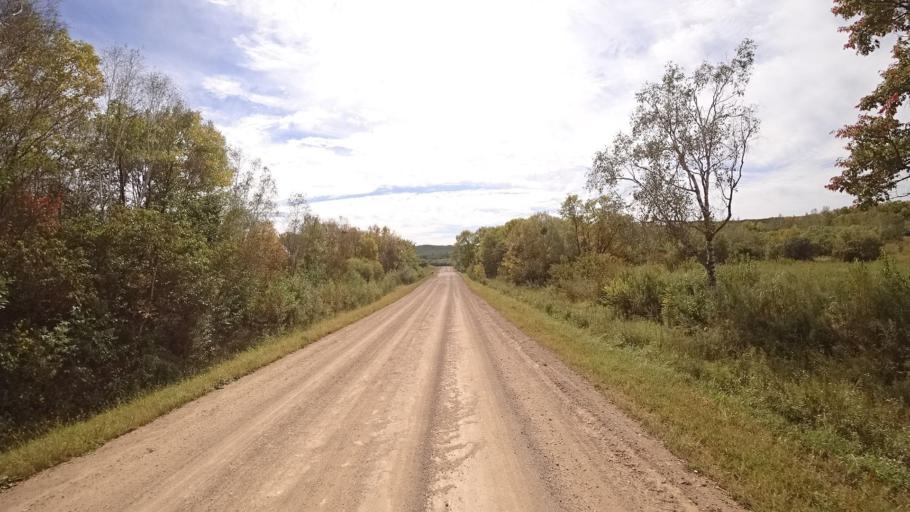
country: RU
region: Primorskiy
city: Yakovlevka
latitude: 44.6216
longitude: 133.5976
